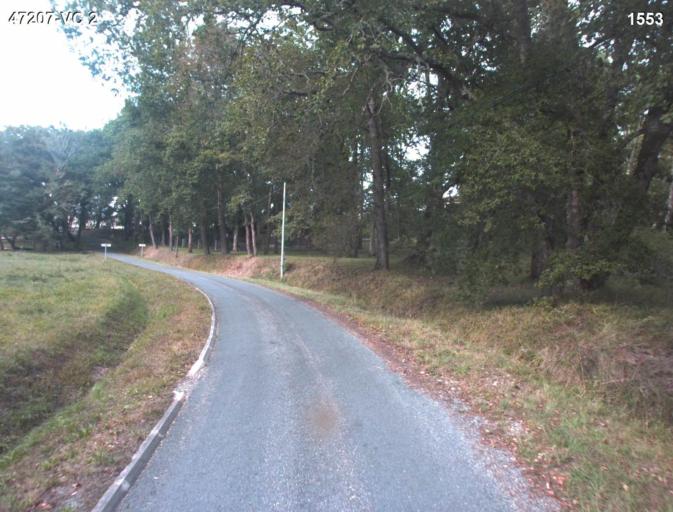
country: FR
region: Aquitaine
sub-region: Departement du Lot-et-Garonne
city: Barbaste
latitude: 44.1901
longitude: 0.2295
